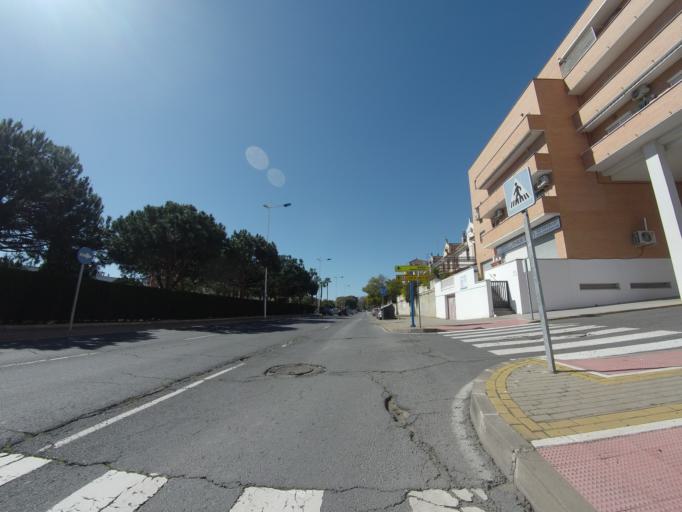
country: ES
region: Andalusia
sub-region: Provincia de Huelva
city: Huelva
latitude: 37.2678
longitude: -6.9357
